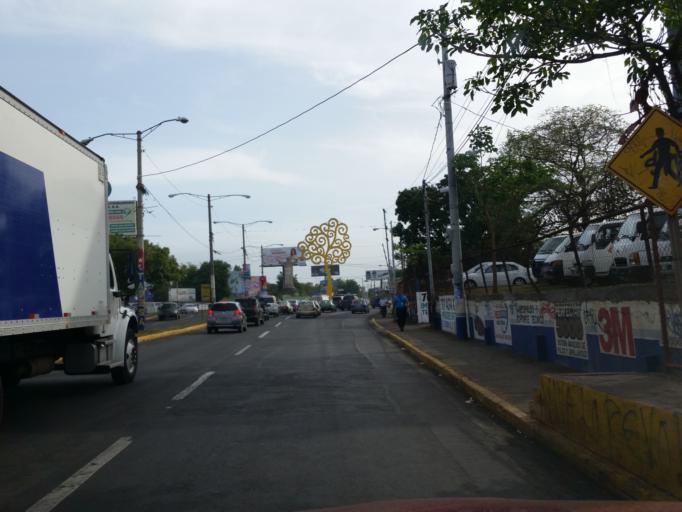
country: NI
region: Managua
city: Managua
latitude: 12.1334
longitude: -86.2564
